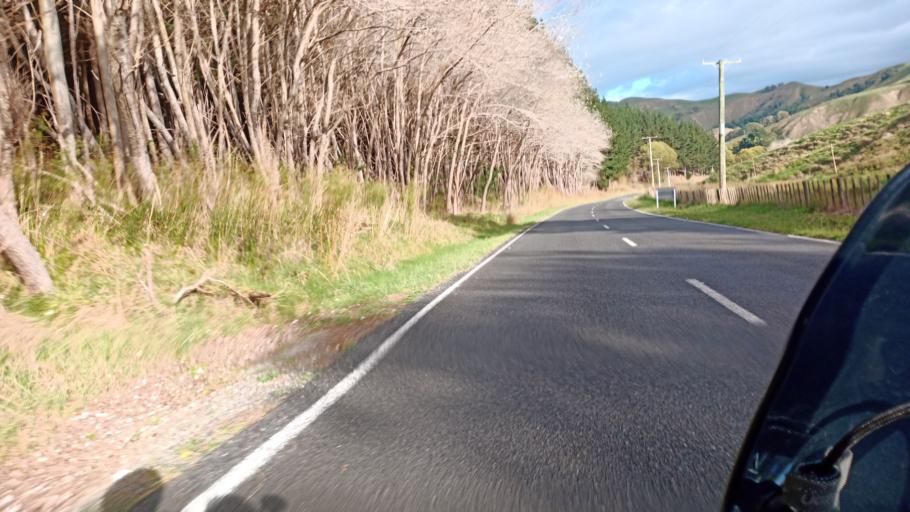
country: NZ
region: Gisborne
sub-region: Gisborne District
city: Gisborne
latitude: -38.5607
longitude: 177.7082
